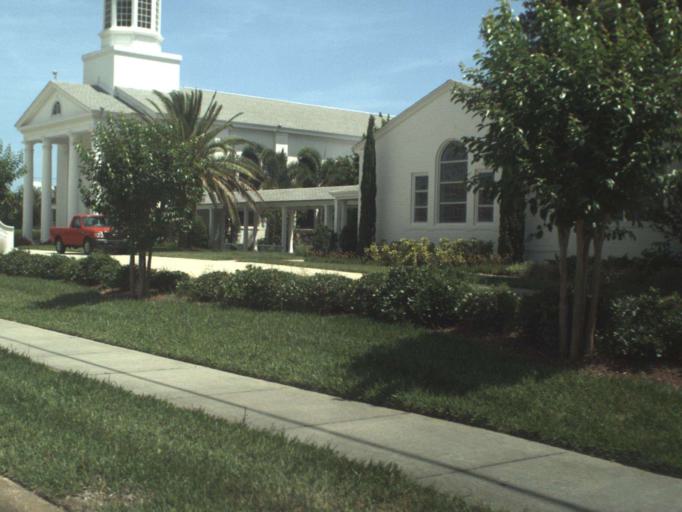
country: US
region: Florida
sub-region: Volusia County
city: Daytona Beach Shores
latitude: 29.1573
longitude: -80.9756
